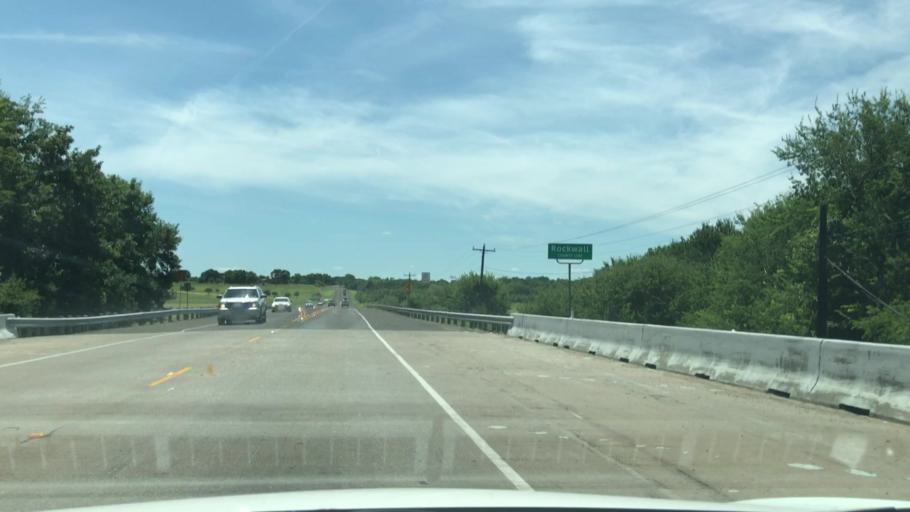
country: US
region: Texas
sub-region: Rockwall County
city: Rockwall
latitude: 32.9824
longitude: -96.4668
